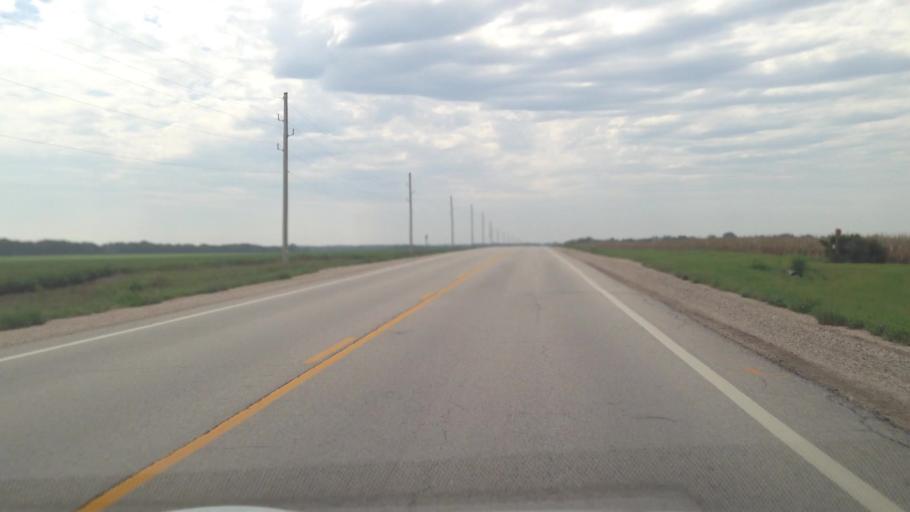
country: US
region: Kansas
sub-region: Anderson County
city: Garnett
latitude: 38.0562
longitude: -95.1695
